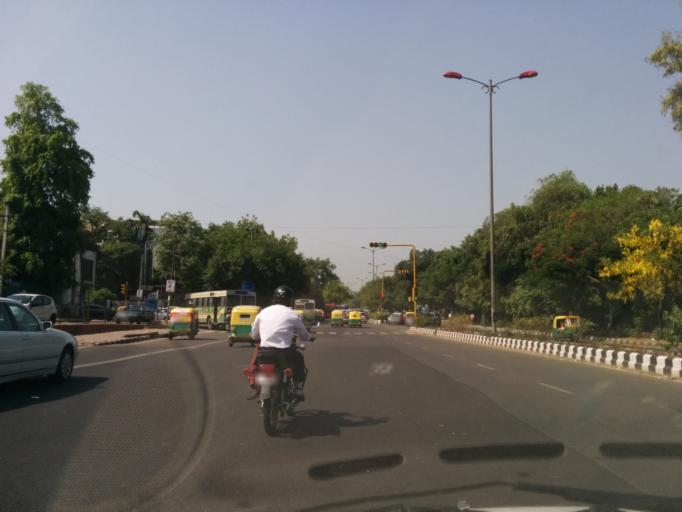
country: IN
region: NCT
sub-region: New Delhi
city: New Delhi
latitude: 28.5542
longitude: 77.2056
